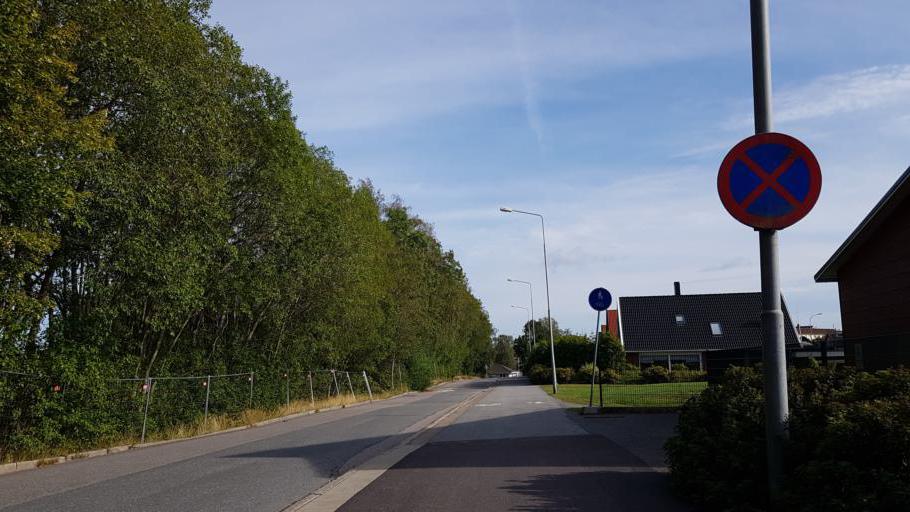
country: SE
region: Vaestra Goetaland
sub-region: Molndal
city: Moelndal
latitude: 57.6643
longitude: 12.0370
